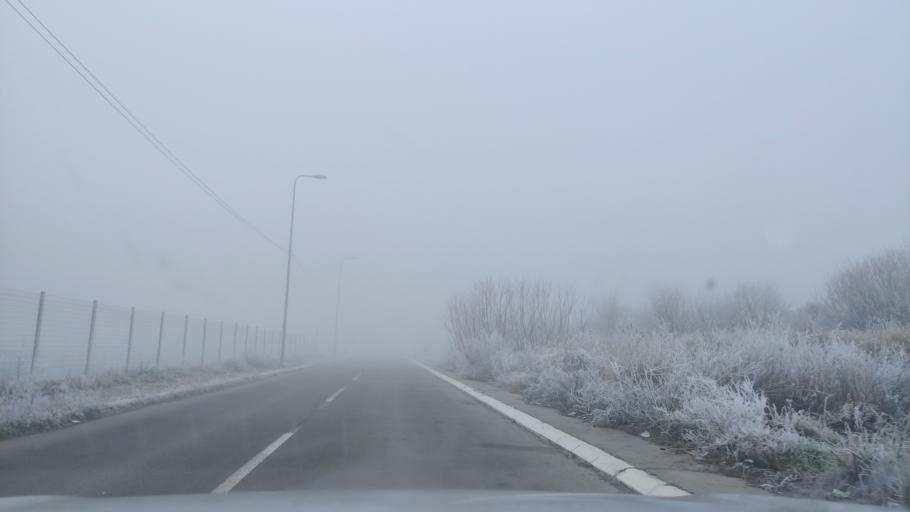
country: RS
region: Central Serbia
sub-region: Belgrade
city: Zemun
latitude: 44.8666
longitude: 20.3502
